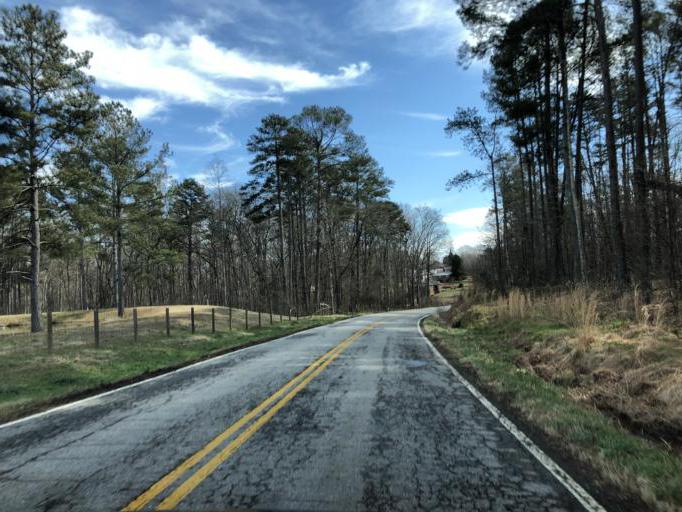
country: US
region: South Carolina
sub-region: Spartanburg County
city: Mayo
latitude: 35.0442
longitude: -81.8854
